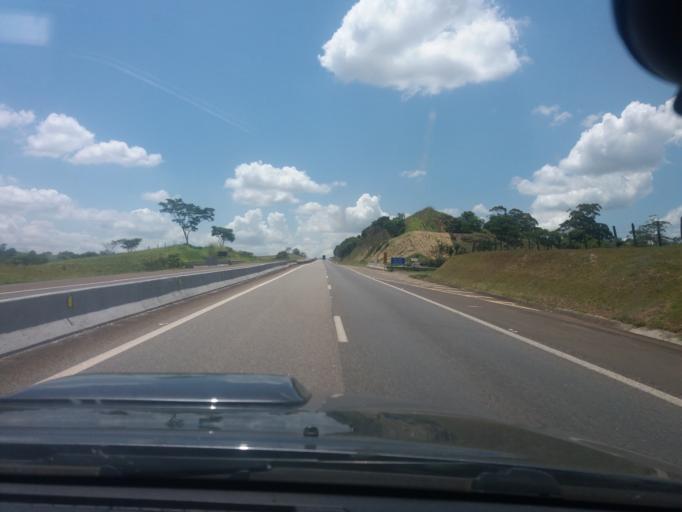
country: BR
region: Sao Paulo
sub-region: Itapetininga
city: Itapetininga
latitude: -23.4864
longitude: -47.9733
